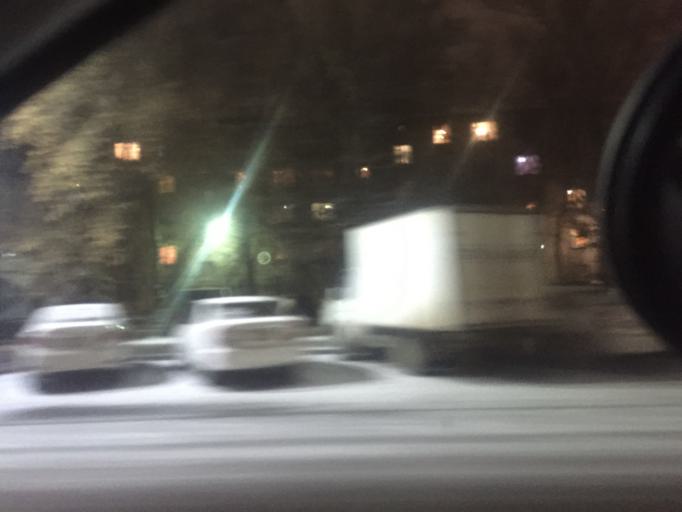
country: KZ
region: Astana Qalasy
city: Astana
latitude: 51.1808
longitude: 71.4174
